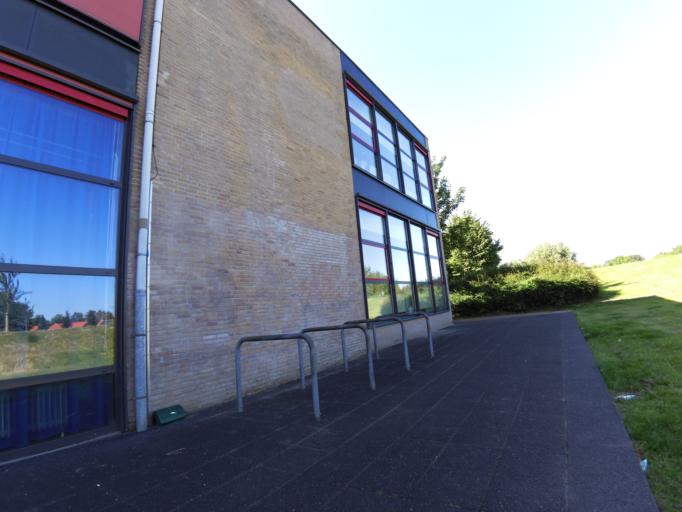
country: NL
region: South Holland
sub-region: Gemeente Hellevoetsluis
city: Hellevoetsluis
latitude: 51.8265
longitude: 4.1321
